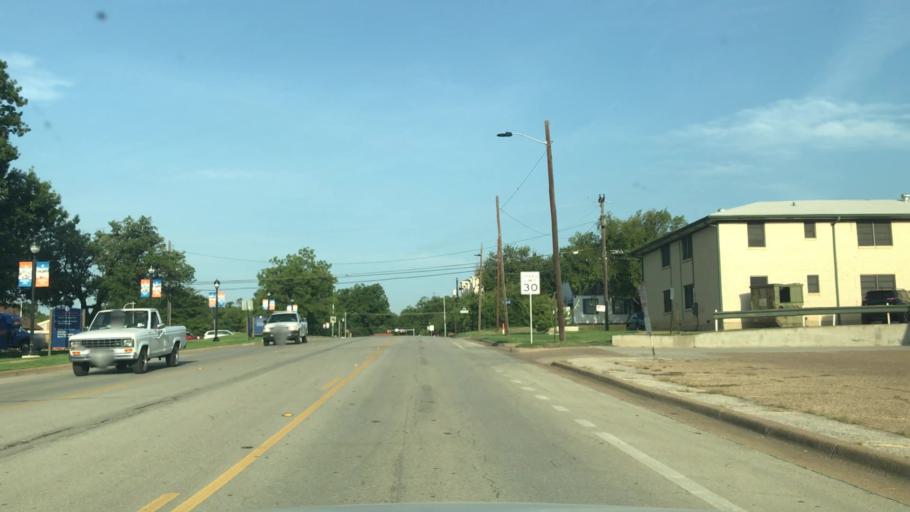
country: US
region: Texas
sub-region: Tarrant County
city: Arlington
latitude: 32.7344
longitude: -97.1209
